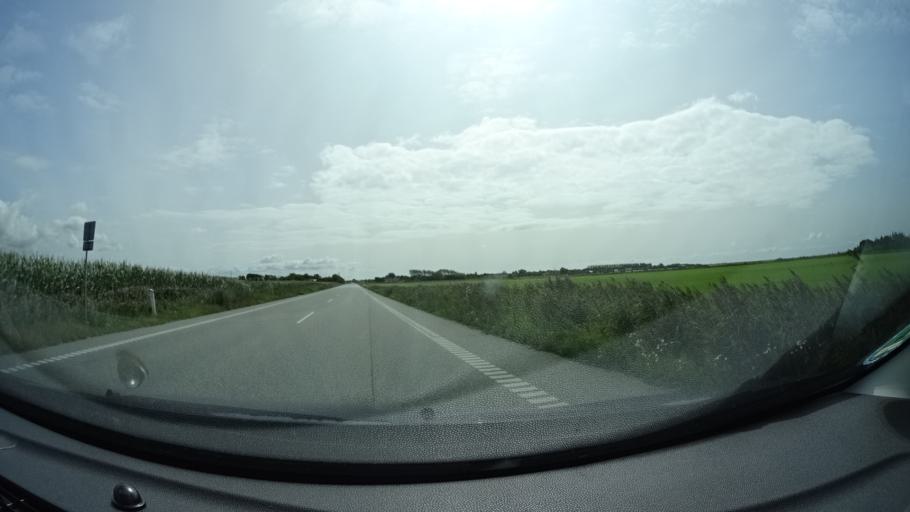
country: DE
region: Schleswig-Holstein
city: Rodenas
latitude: 54.9782
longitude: 8.6978
